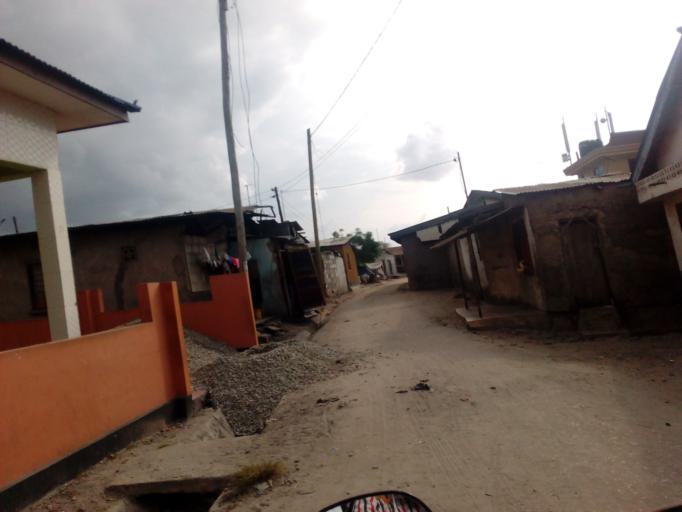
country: TZ
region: Dar es Salaam
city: Dar es Salaam
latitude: -6.8365
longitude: 39.2740
